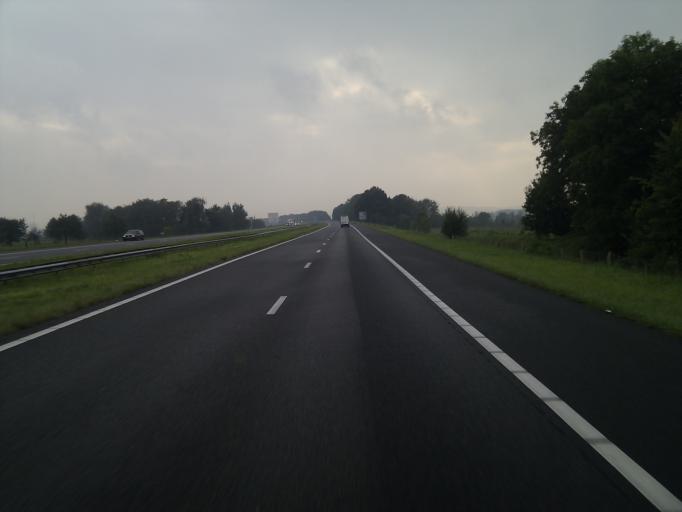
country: NL
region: Limburg
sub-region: Eijsden-Margraten
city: Eijsden
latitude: 50.7656
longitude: 5.7130
